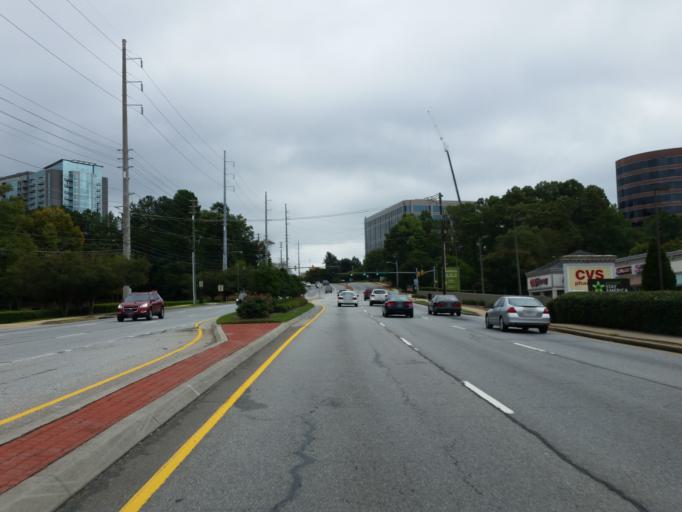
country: US
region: Georgia
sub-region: Cobb County
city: Vinings
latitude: 33.9041
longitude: -84.4611
